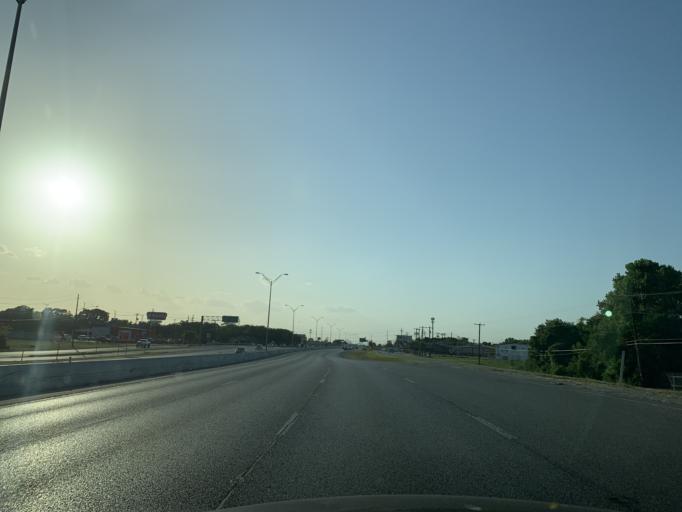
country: US
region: Texas
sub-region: Dallas County
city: Balch Springs
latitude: 32.7089
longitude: -96.6765
